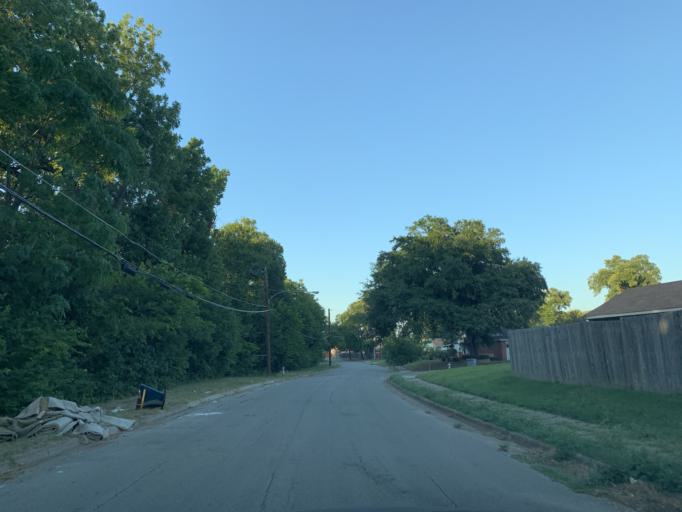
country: US
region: Texas
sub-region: Dallas County
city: Lancaster
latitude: 32.6667
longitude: -96.8040
